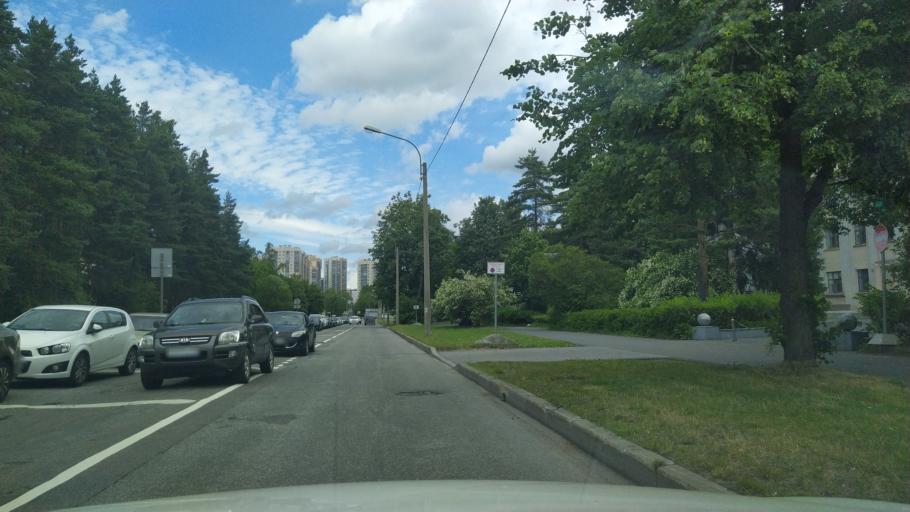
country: RU
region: Leningrad
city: Kalininskiy
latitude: 60.0051
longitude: 30.3839
